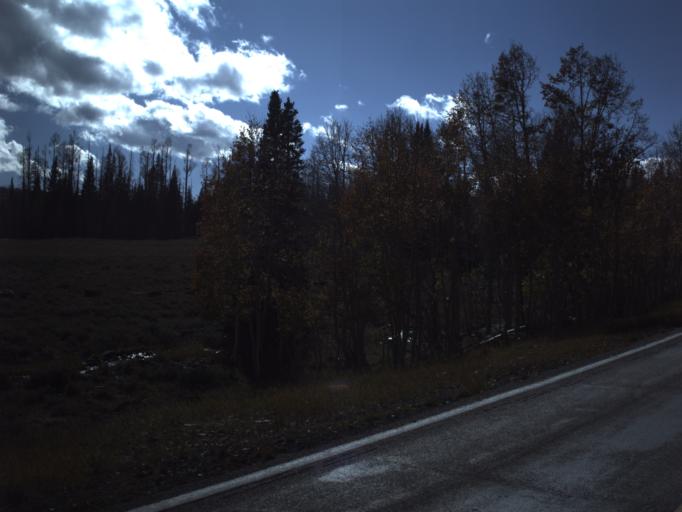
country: US
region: Utah
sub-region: Iron County
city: Parowan
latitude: 37.6551
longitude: -112.7600
